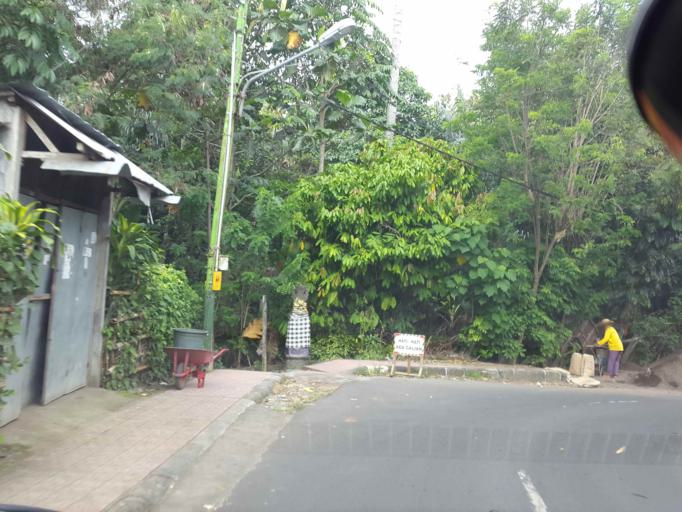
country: ID
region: Bali
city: Klungkung
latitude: -8.5320
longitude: 115.3855
